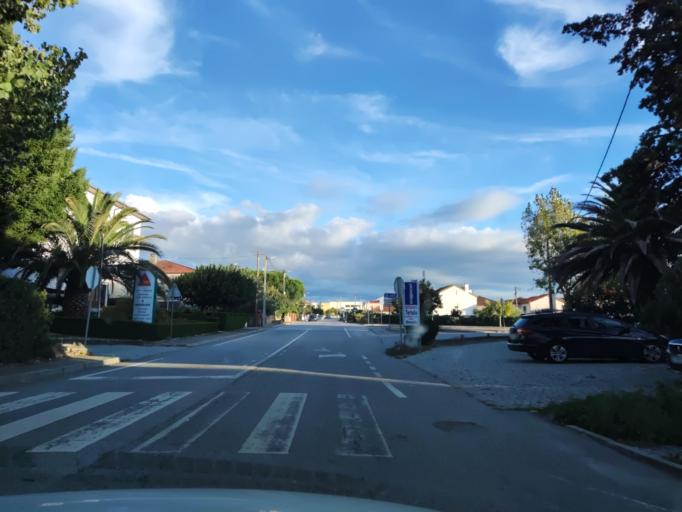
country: ES
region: Castille and Leon
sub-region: Provincia de Salamanca
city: Aldea del Obispo
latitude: 40.7207
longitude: -6.9027
